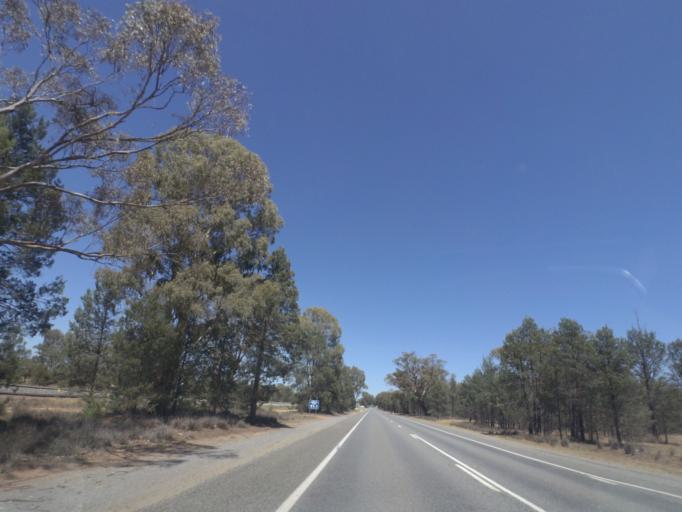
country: AU
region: New South Wales
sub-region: Narrandera
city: Narrandera
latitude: -34.7383
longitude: 146.5780
